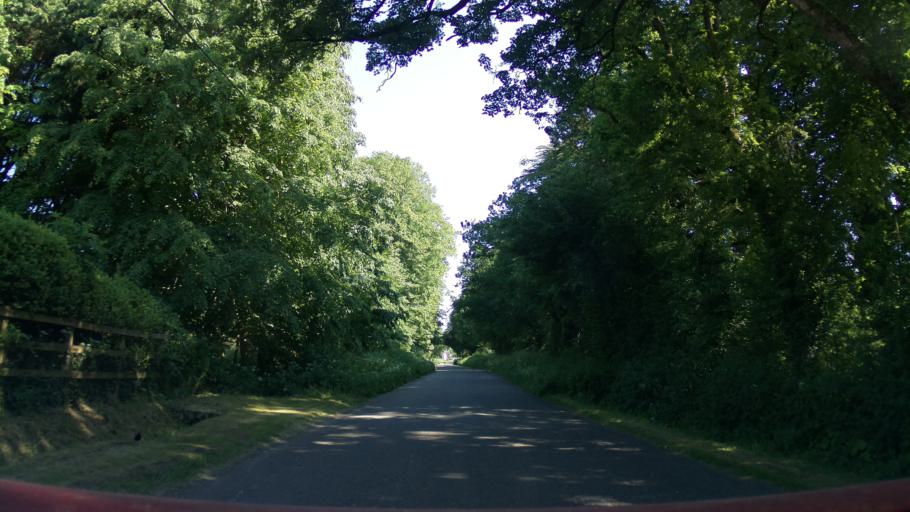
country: GB
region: England
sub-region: Hampshire
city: Abbotts Ann
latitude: 51.2527
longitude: -1.5760
